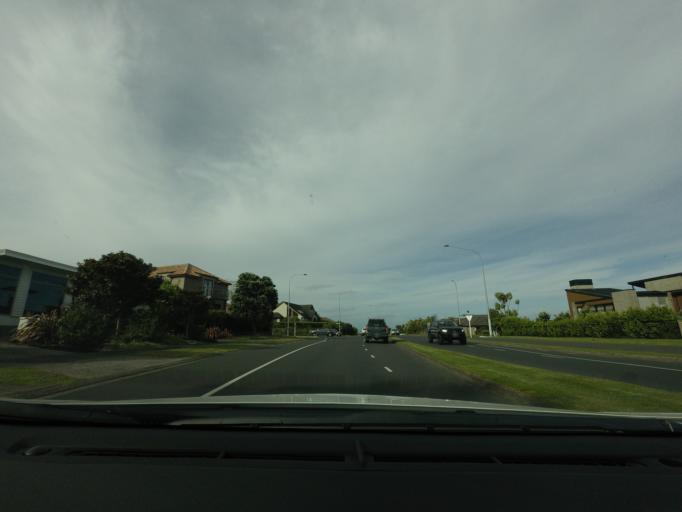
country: NZ
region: Auckland
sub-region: Auckland
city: Rothesay Bay
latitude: -36.5881
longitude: 174.6807
